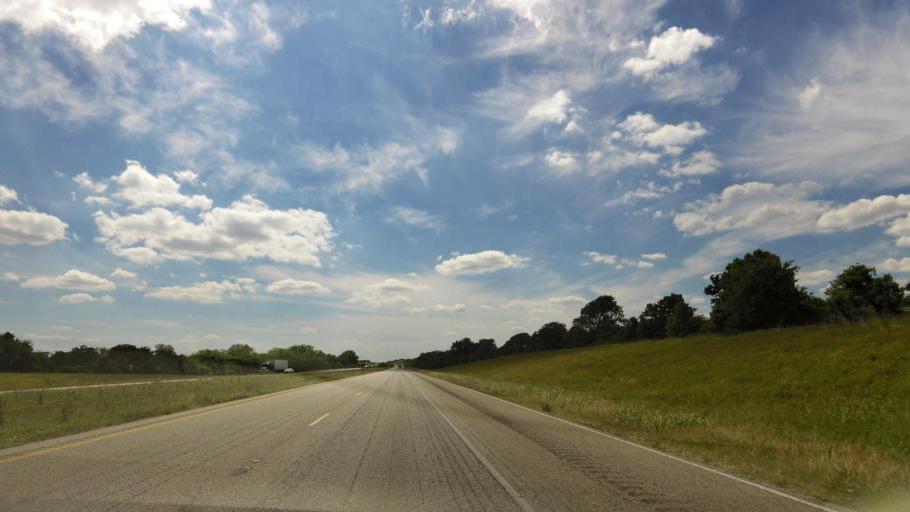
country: US
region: Texas
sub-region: Gonzales County
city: Waelder
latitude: 29.6634
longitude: -97.3755
